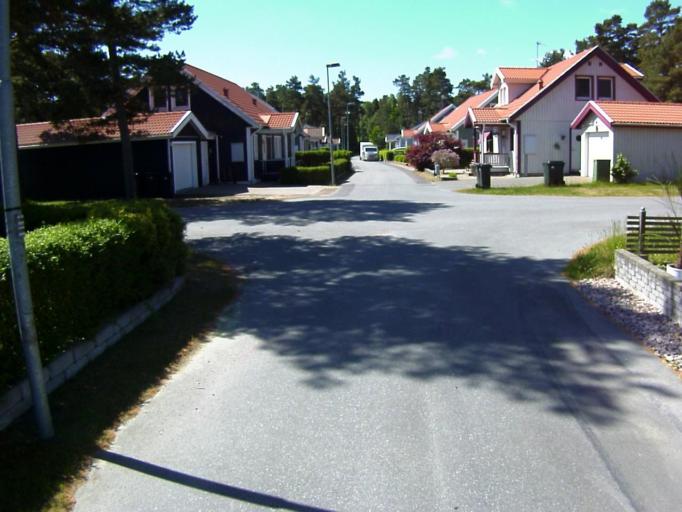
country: SE
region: Skane
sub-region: Kristianstads Kommun
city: Ahus
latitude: 55.9422
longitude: 14.2985
